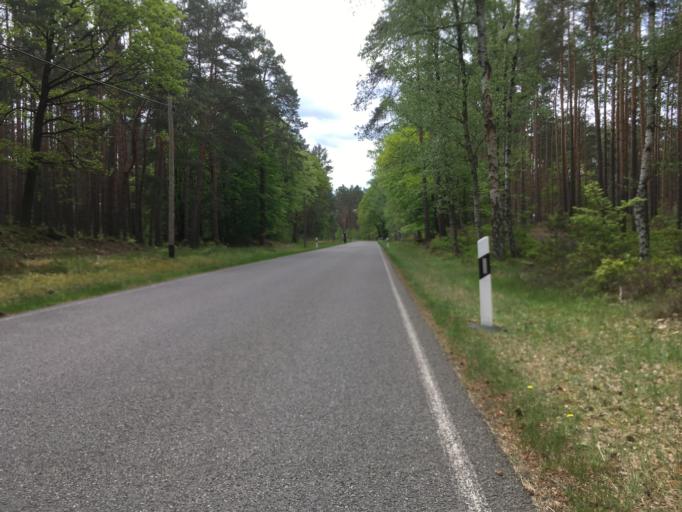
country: DE
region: Brandenburg
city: Joachimsthal
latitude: 52.9964
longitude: 13.7430
